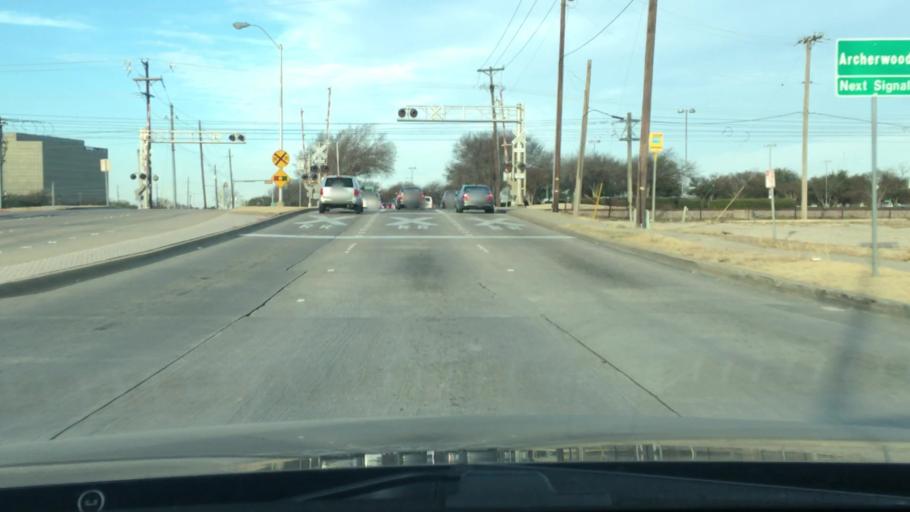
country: US
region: Texas
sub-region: Collin County
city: Plano
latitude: 33.0315
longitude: -96.7001
